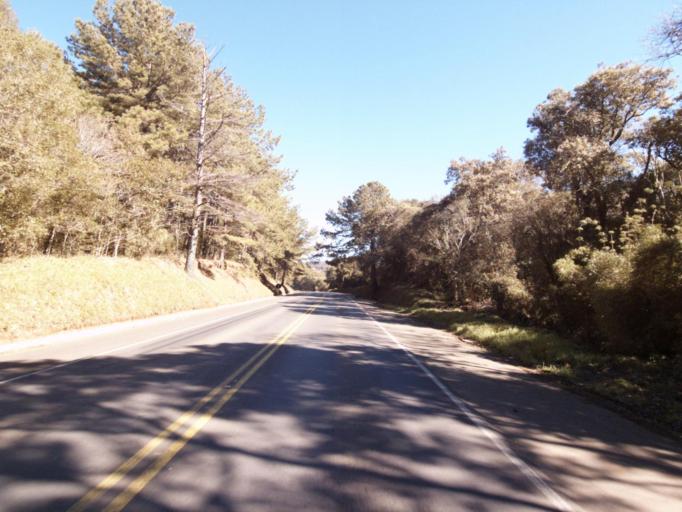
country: BR
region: Santa Catarina
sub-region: Joacaba
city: Joacaba
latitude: -26.9742
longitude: -51.7663
